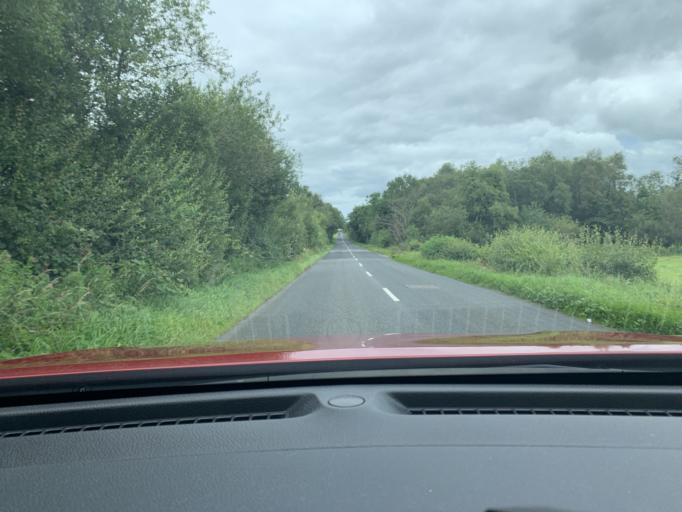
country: GB
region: Northern Ireland
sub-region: Fermanagh District
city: Enniskillen
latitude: 54.2868
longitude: -7.6991
